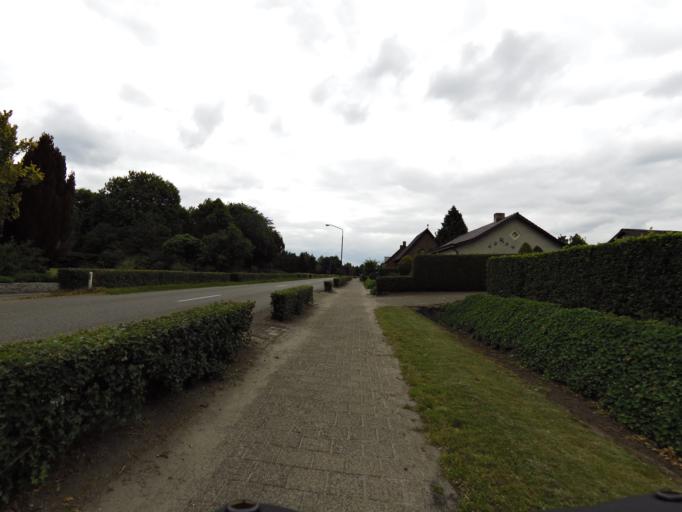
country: NL
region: North Brabant
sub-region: Gemeente Zundert
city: Zundert
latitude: 51.5143
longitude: 4.7127
